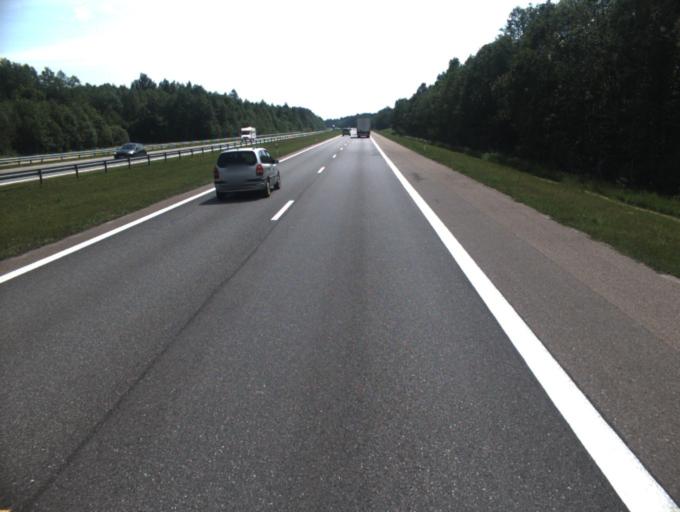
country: LT
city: Rietavas
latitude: 55.6550
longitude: 21.7829
